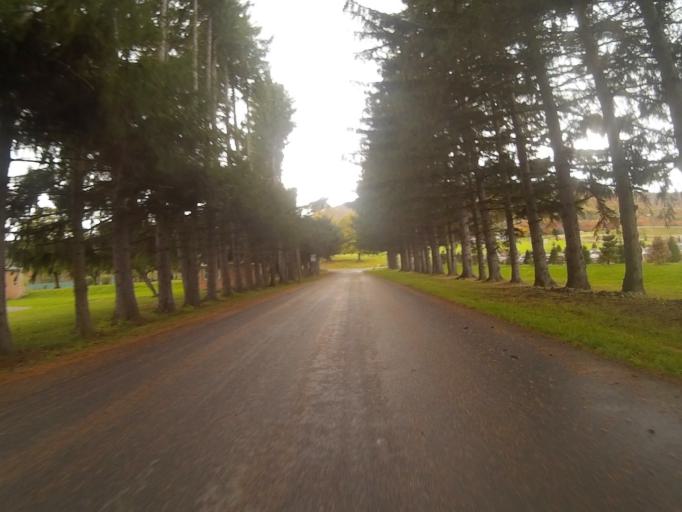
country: US
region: Pennsylvania
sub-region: Centre County
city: Boalsburg
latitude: 40.7780
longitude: -77.7702
